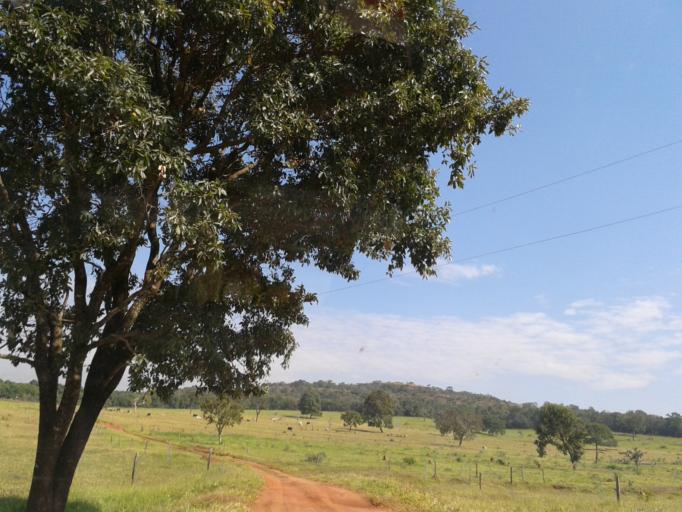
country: BR
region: Minas Gerais
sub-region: Campina Verde
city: Campina Verde
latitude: -19.3906
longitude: -49.6319
